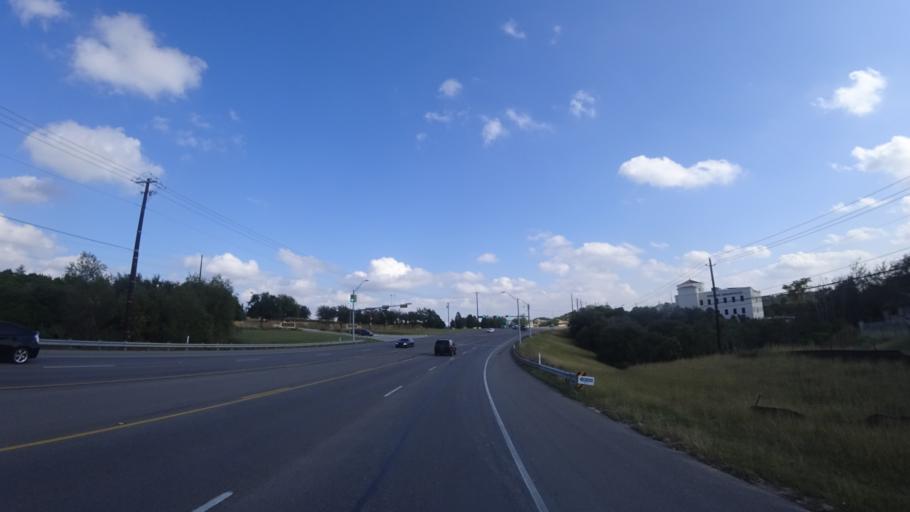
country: US
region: Texas
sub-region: Travis County
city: Lost Creek
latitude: 30.3183
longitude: -97.8628
